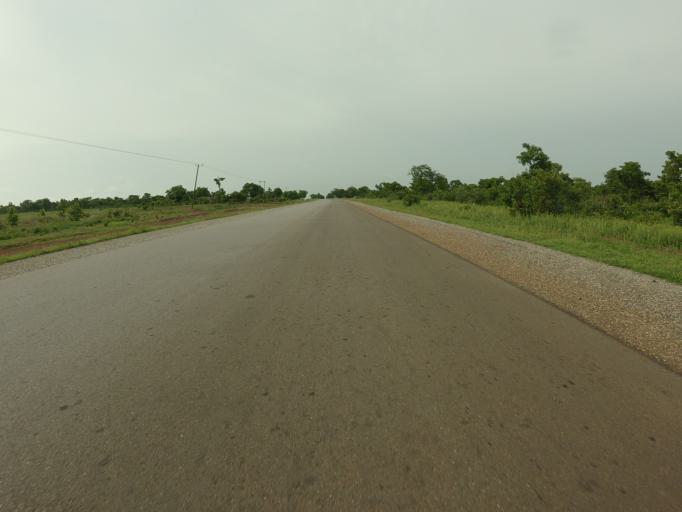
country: GH
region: Northern
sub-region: Yendi
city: Yendi
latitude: 9.6444
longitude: -0.0672
